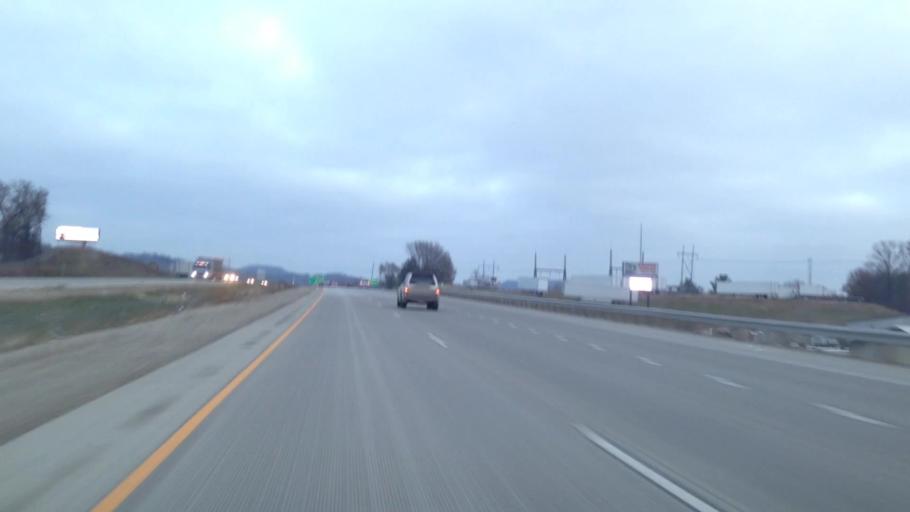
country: US
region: Wisconsin
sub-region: La Crosse County
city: Onalaska
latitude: 43.8685
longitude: -91.2234
